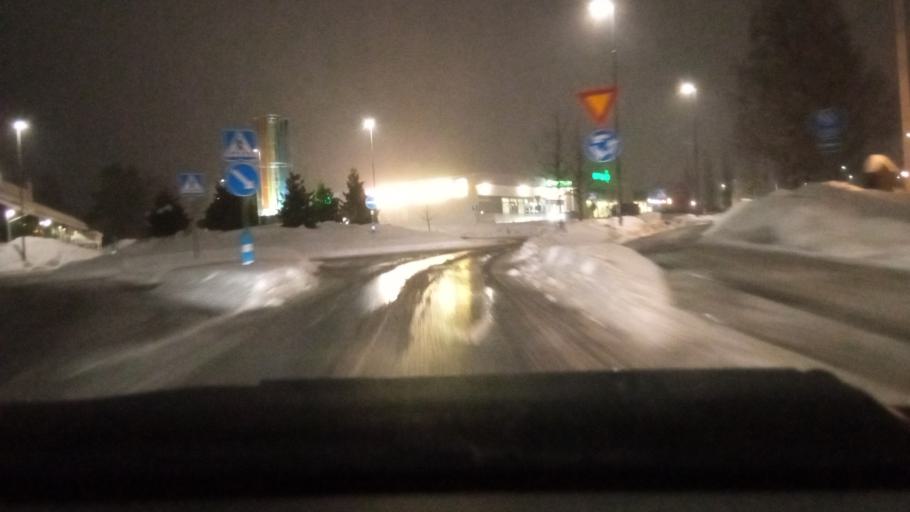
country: FI
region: Southern Ostrobothnia
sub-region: Jaerviseutu
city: Alajaervi
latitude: 63.0016
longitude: 23.8142
